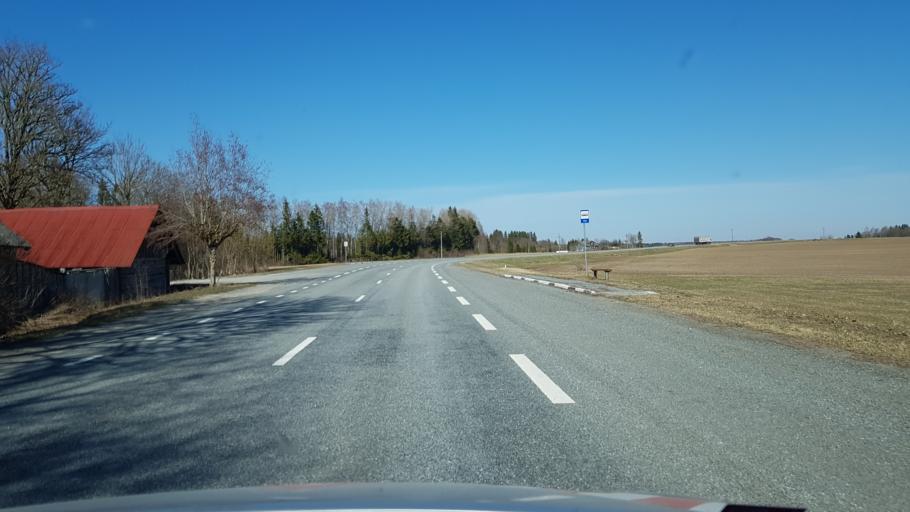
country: EE
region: Jaervamaa
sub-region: Jaerva-Jaani vald
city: Jarva-Jaani
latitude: 59.0677
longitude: 25.9332
